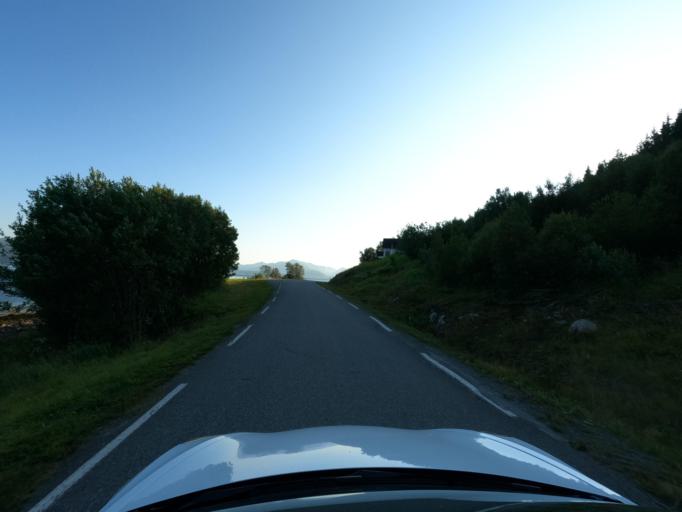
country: NO
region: Nordland
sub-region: Ballangen
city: Ballangen
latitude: 68.4624
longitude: 16.7679
